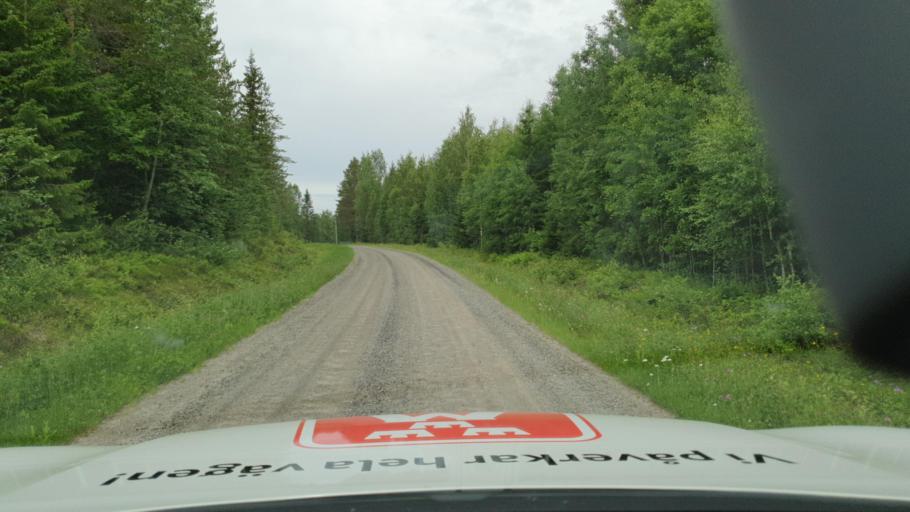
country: SE
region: Vaesterbotten
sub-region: Robertsfors Kommun
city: Robertsfors
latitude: 64.1983
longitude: 20.7073
